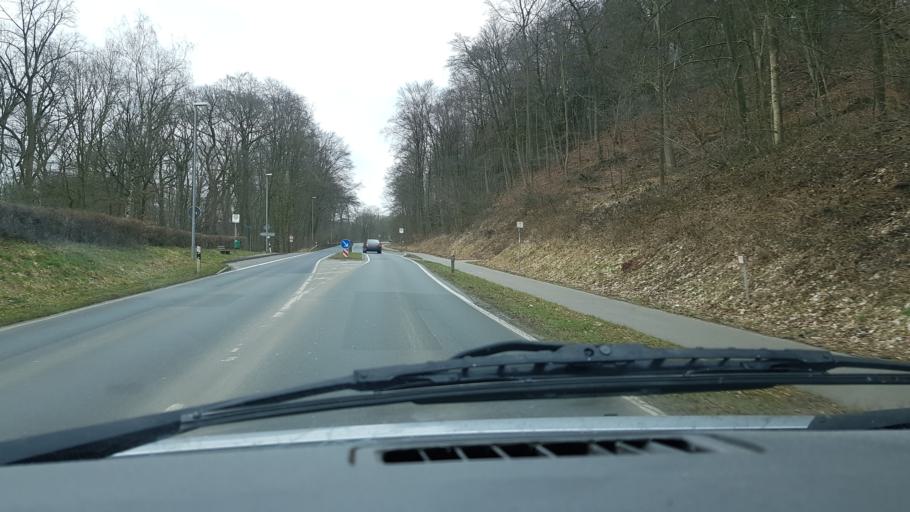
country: DE
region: North Rhine-Westphalia
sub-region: Regierungsbezirk Dusseldorf
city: Kleve
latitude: 51.8006
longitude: 6.1067
